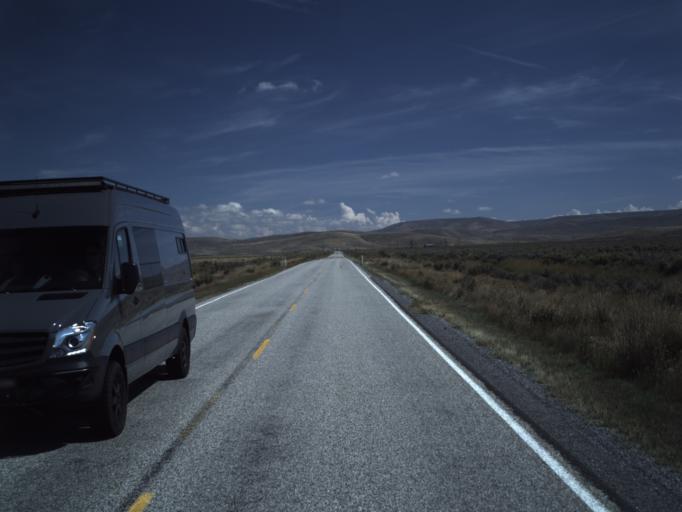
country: US
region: Utah
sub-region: Rich County
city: Randolph
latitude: 41.7780
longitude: -111.0637
